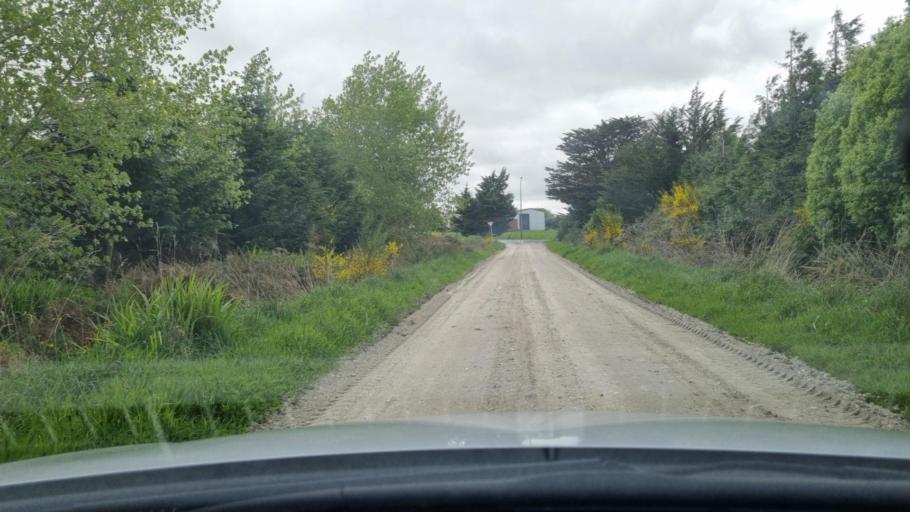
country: NZ
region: Southland
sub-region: Invercargill City
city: Invercargill
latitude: -46.4333
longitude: 168.3896
